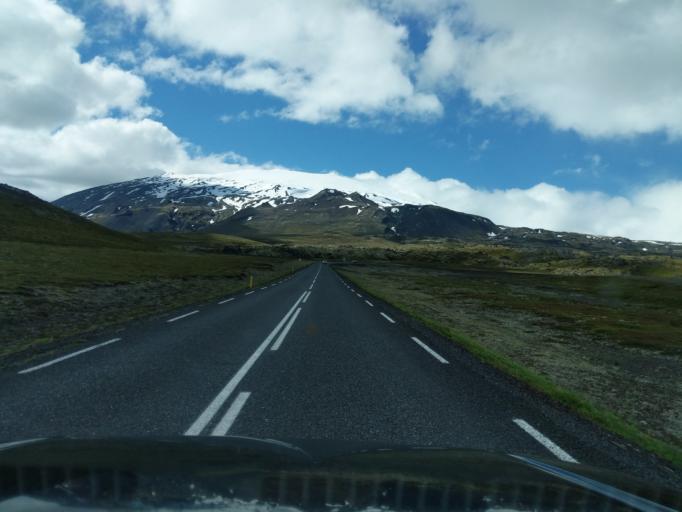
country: IS
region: West
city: Olafsvik
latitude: 64.7599
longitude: -23.6725
